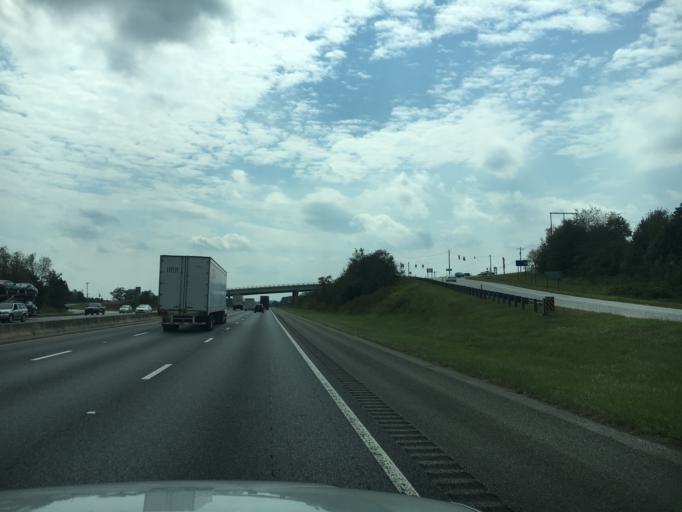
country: US
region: South Carolina
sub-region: Anderson County
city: Powdersville
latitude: 34.7624
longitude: -82.4731
